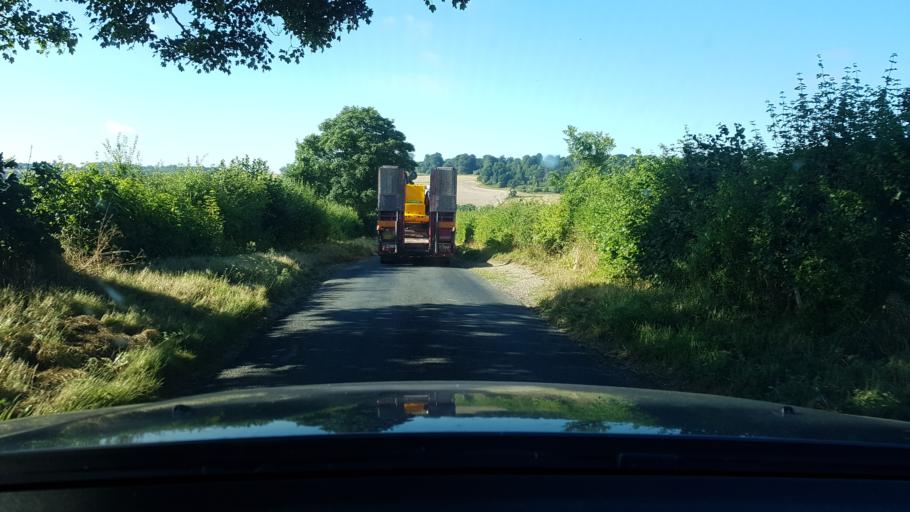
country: GB
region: England
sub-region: Wiltshire
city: Ramsbury
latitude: 51.4440
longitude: -1.5795
